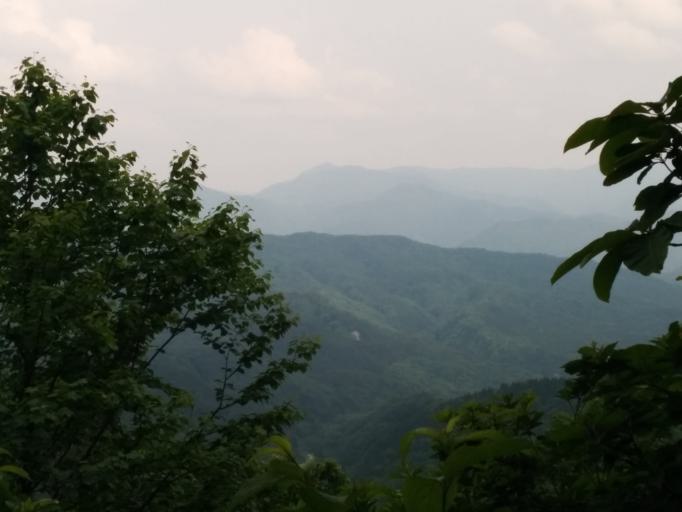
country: JP
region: Aomori
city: Hirosaki
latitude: 40.5539
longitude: 140.1653
